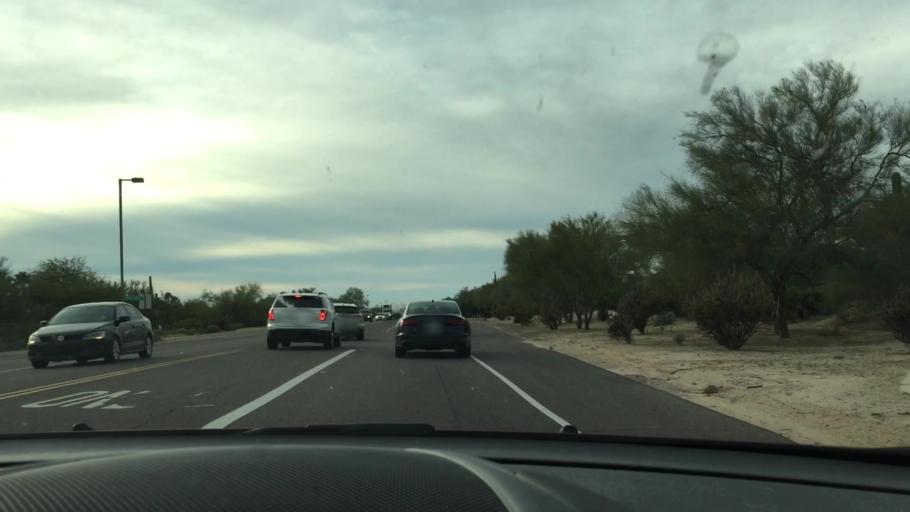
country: US
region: Arizona
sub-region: Maricopa County
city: Carefree
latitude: 33.6987
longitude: -111.9098
